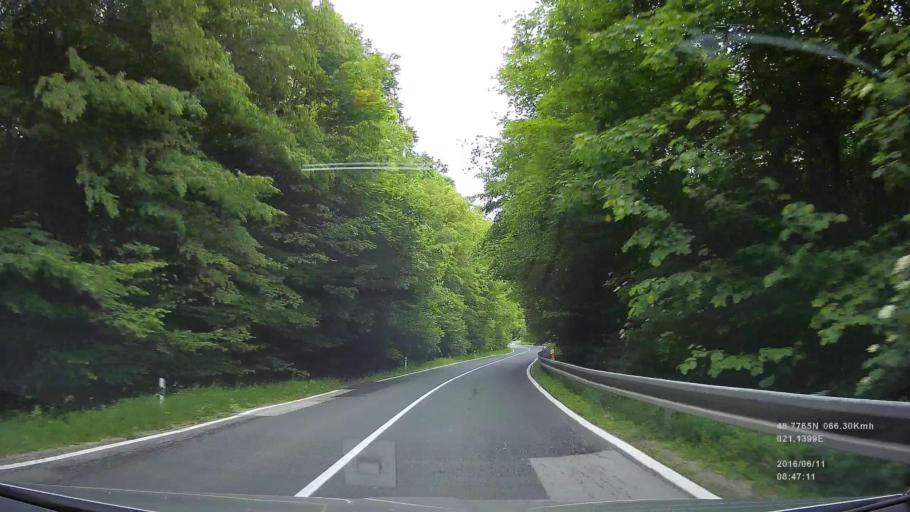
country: SK
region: Kosicky
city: Kosice
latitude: 48.7639
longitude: 21.1740
